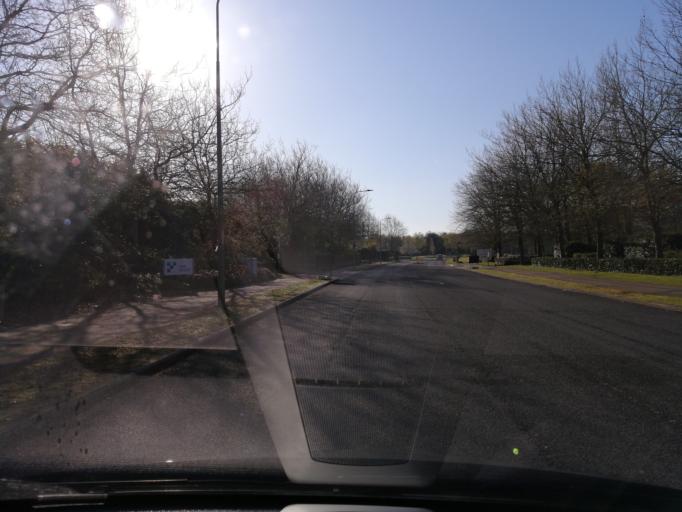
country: GB
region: England
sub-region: Peterborough
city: Castor
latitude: 52.5533
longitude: -0.3156
